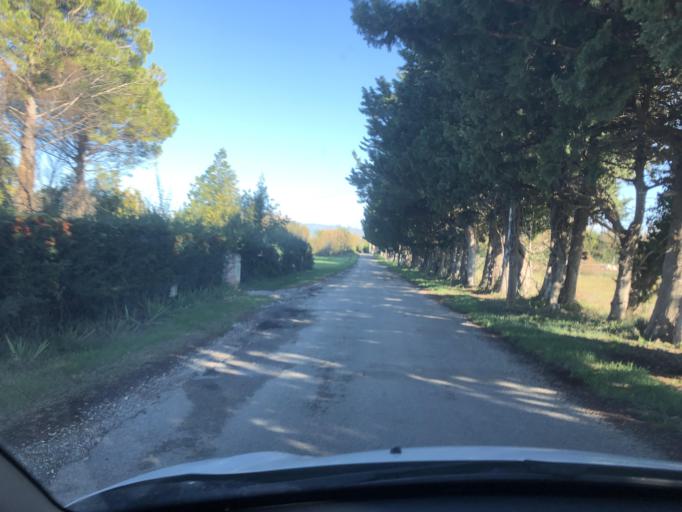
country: FR
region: Provence-Alpes-Cote d'Azur
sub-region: Departement du Vaucluse
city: Althen-des-Paluds
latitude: 43.9819
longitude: 4.9865
